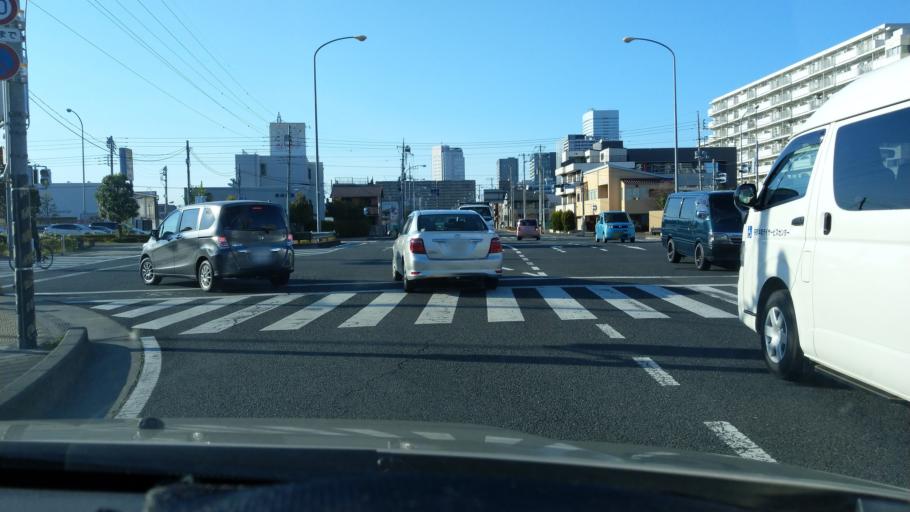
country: JP
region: Saitama
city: Yono
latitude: 35.8967
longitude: 139.6213
